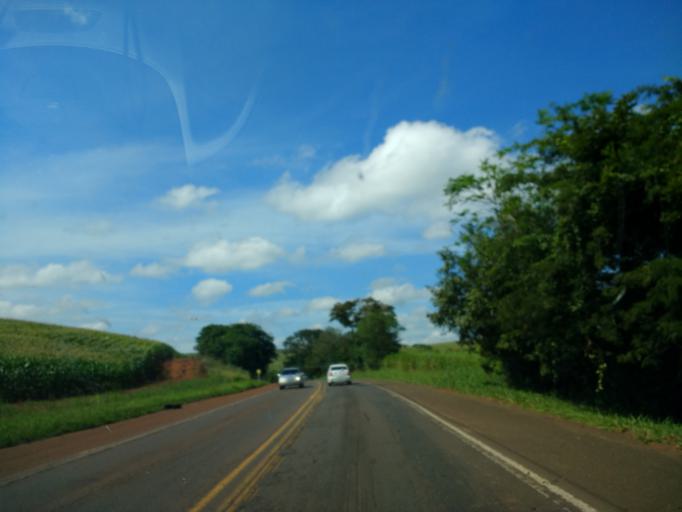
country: BR
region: Parana
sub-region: Cianorte
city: Cianorte
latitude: -23.6562
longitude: -52.5114
